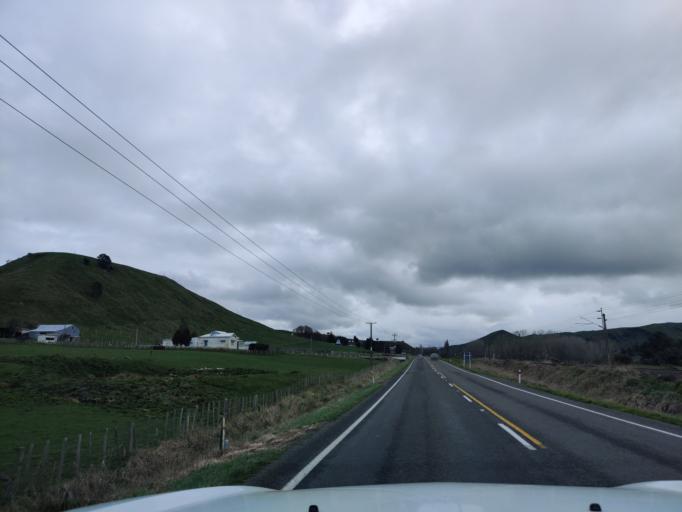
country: NZ
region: Manawatu-Wanganui
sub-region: Ruapehu District
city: Waiouru
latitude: -39.7098
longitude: 175.8358
